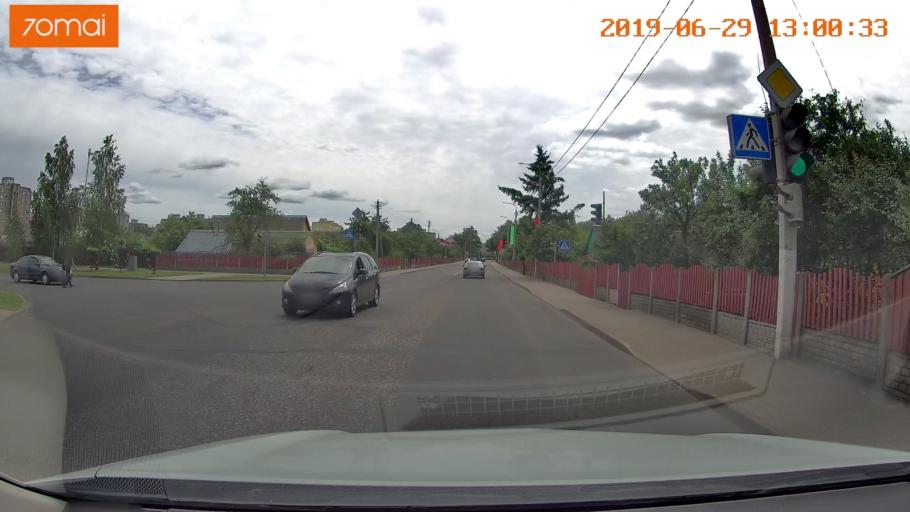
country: BY
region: Minsk
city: Slutsk
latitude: 53.0439
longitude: 27.5574
